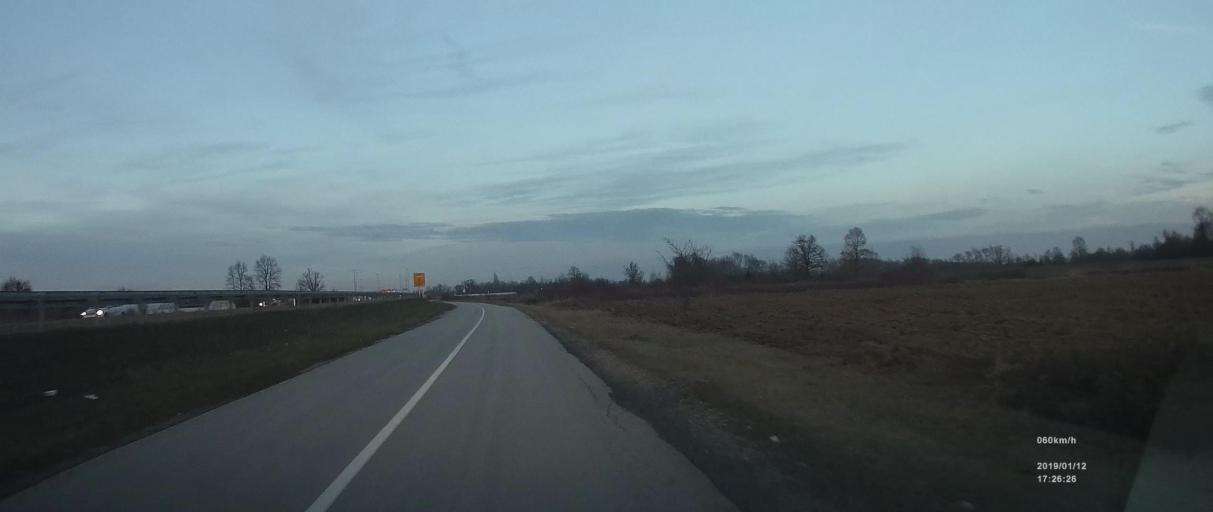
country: HR
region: Zagrebacka
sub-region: Grad Velika Gorica
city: Velika Gorica
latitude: 45.7370
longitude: 16.1036
